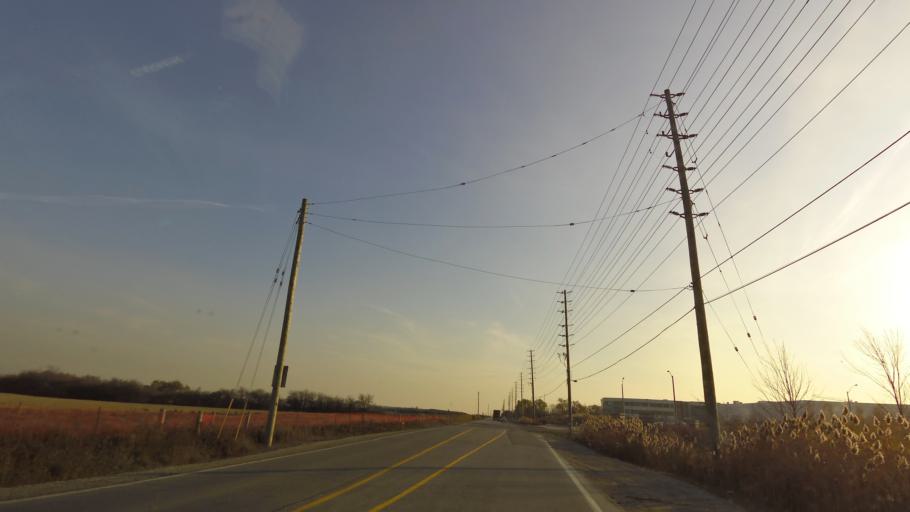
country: CA
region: Ontario
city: Brampton
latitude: 43.7949
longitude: -79.6531
